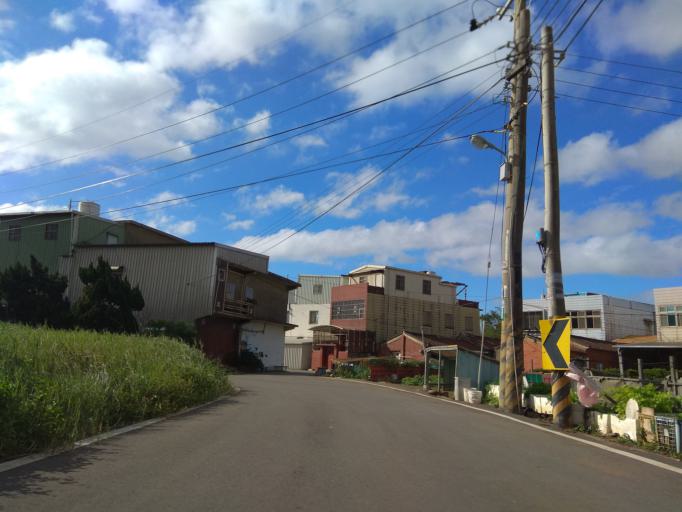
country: TW
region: Taiwan
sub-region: Hsinchu
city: Zhubei
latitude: 24.9722
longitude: 121.0724
